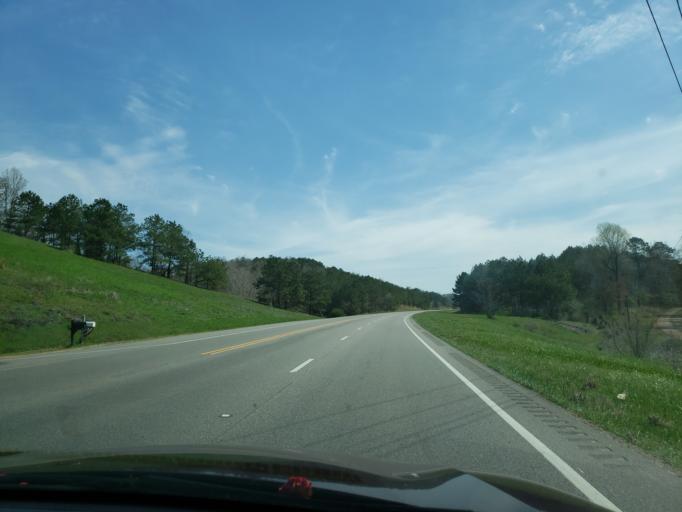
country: US
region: Alabama
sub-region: Autauga County
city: Prattville
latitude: 32.4329
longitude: -86.5636
